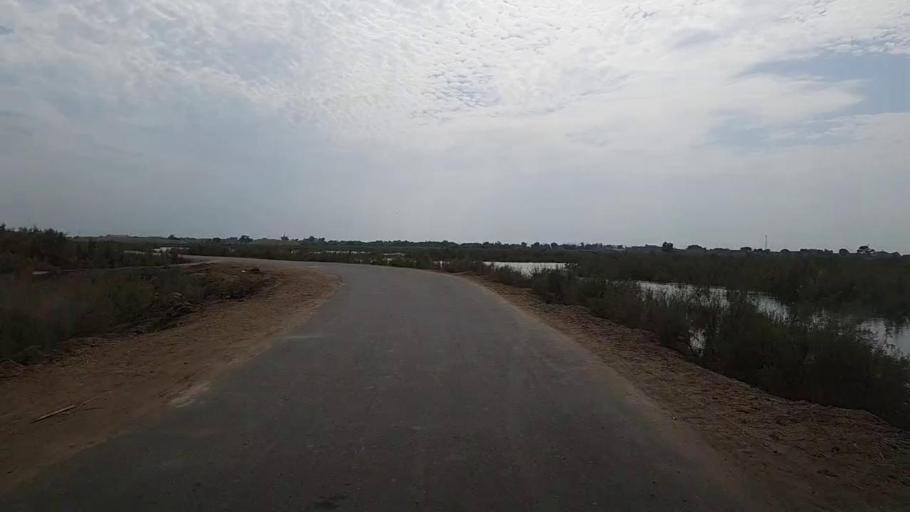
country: PK
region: Sindh
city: Thul
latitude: 28.2643
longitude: 68.7791
